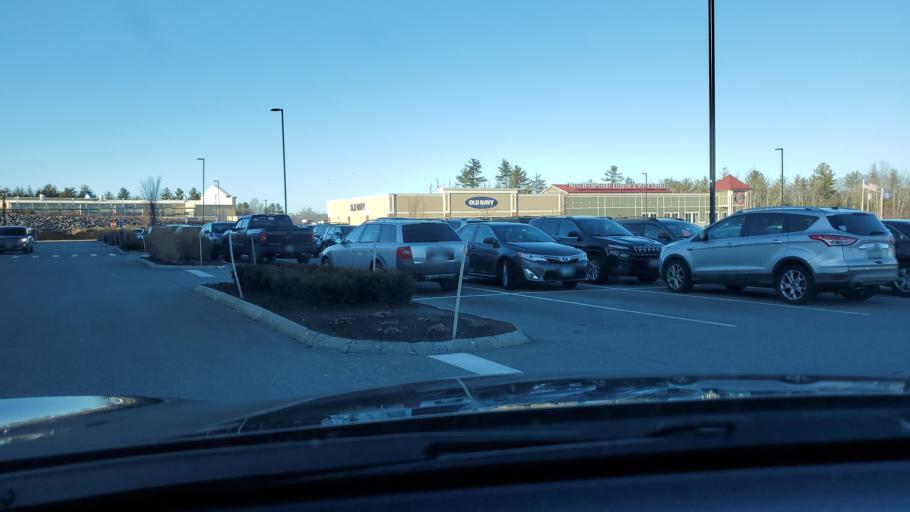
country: US
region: New Hampshire
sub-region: Strafford County
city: Rochester
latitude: 43.3322
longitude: -71.0110
